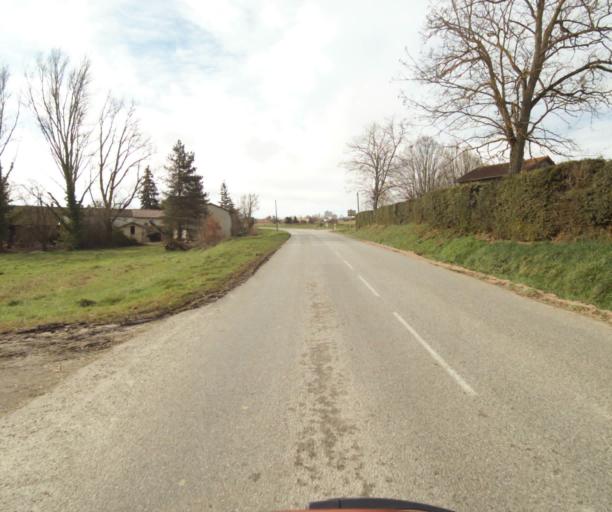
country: FR
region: Midi-Pyrenees
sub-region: Departement de l'Ariege
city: Pamiers
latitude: 43.1294
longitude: 1.5518
